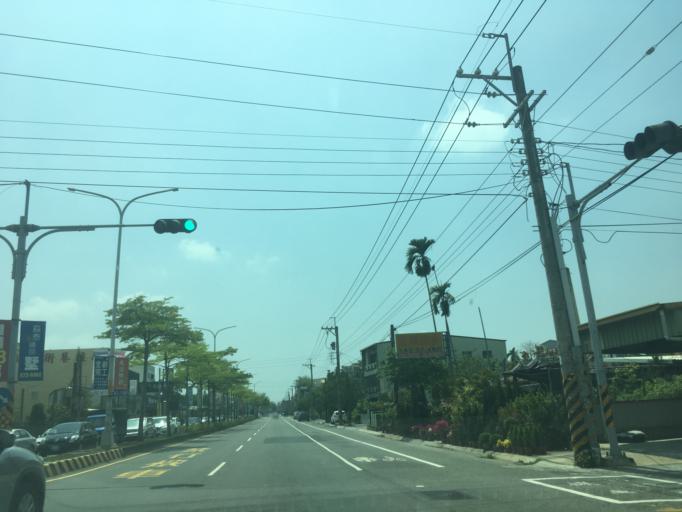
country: TW
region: Taiwan
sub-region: Nantou
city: Nantou
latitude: 23.9103
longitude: 120.5423
